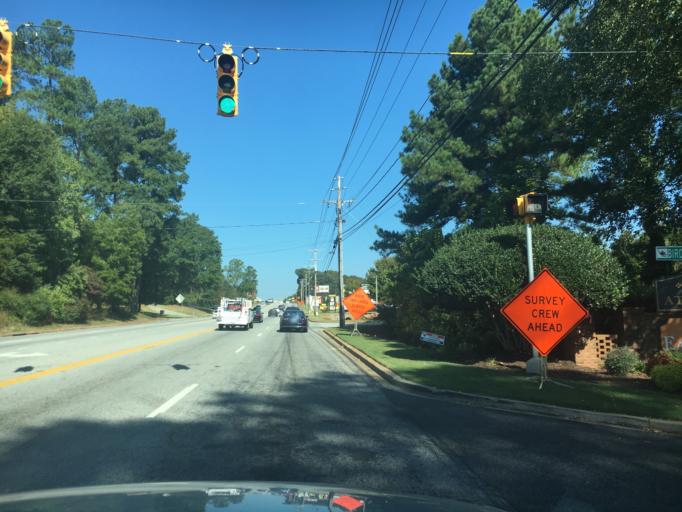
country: US
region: South Carolina
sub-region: Spartanburg County
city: Valley Falls
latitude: 35.0285
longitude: -81.9666
